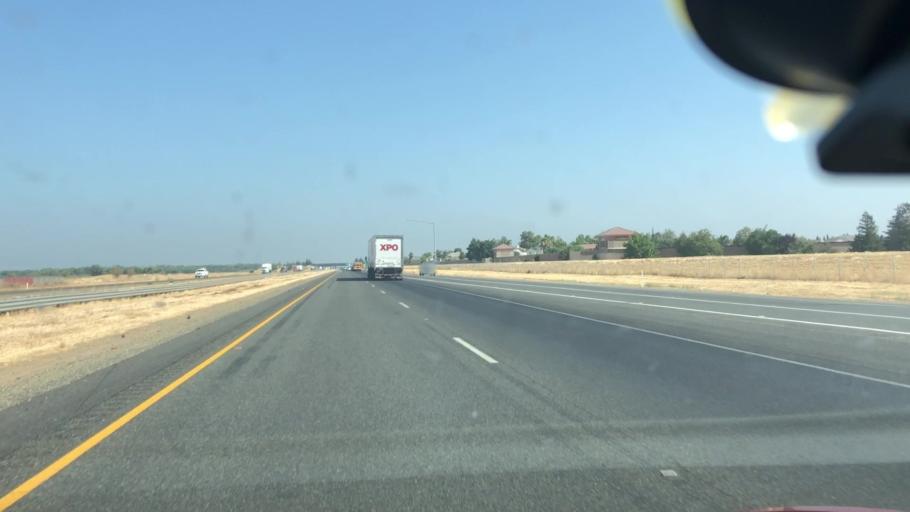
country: US
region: California
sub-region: Sacramento County
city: Laguna
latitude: 38.4133
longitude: -121.4845
